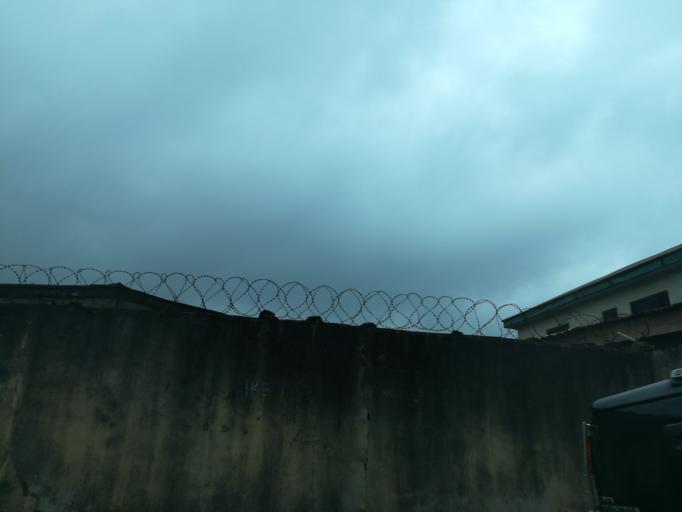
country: NG
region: Rivers
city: Port Harcourt
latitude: 4.8161
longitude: 7.0118
